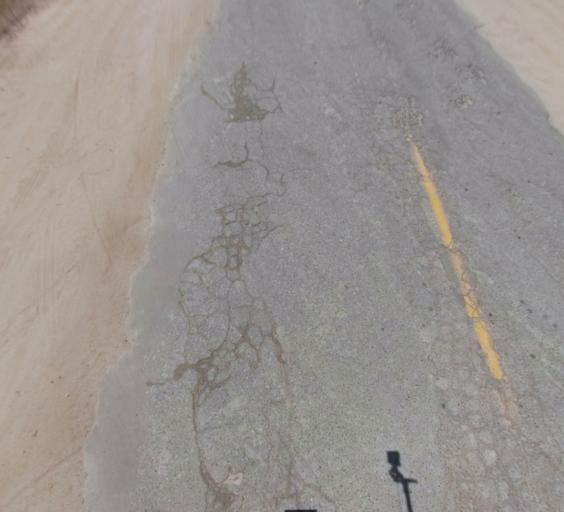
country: US
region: California
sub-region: Madera County
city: Parksdale
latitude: 36.9288
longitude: -120.0013
